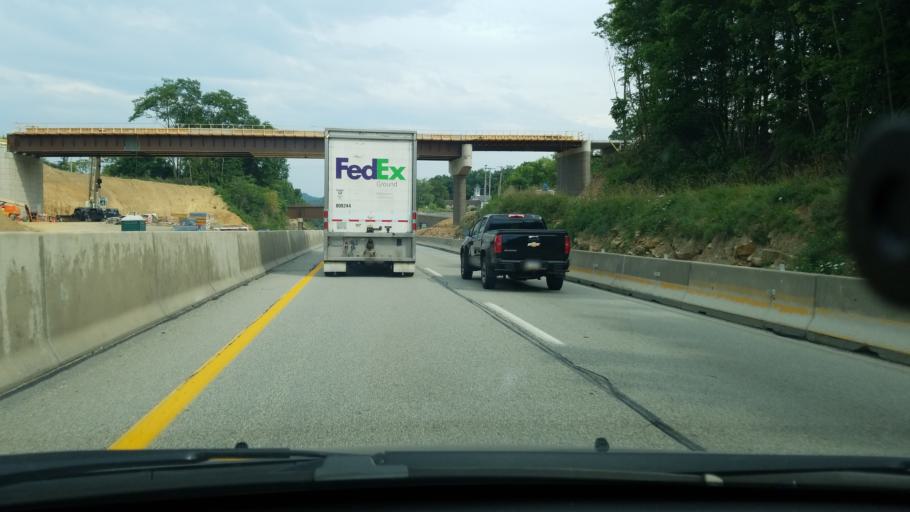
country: US
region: Pennsylvania
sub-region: Beaver County
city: Big Beaver
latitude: 40.8166
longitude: -80.3300
